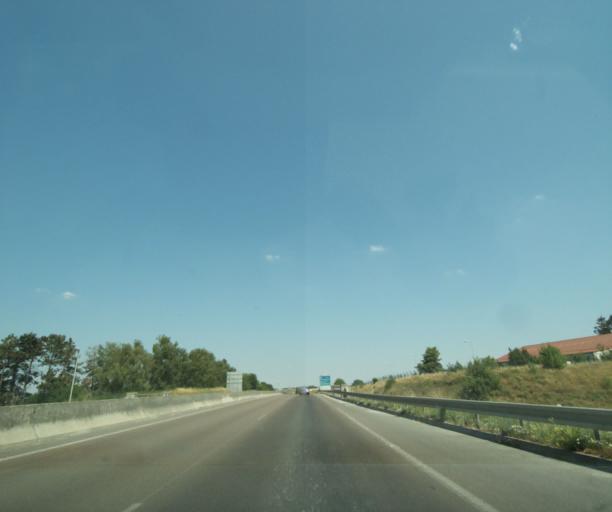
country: FR
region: Champagne-Ardenne
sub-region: Departement de la Marne
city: Saint-Memmie
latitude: 48.9688
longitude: 4.3826
